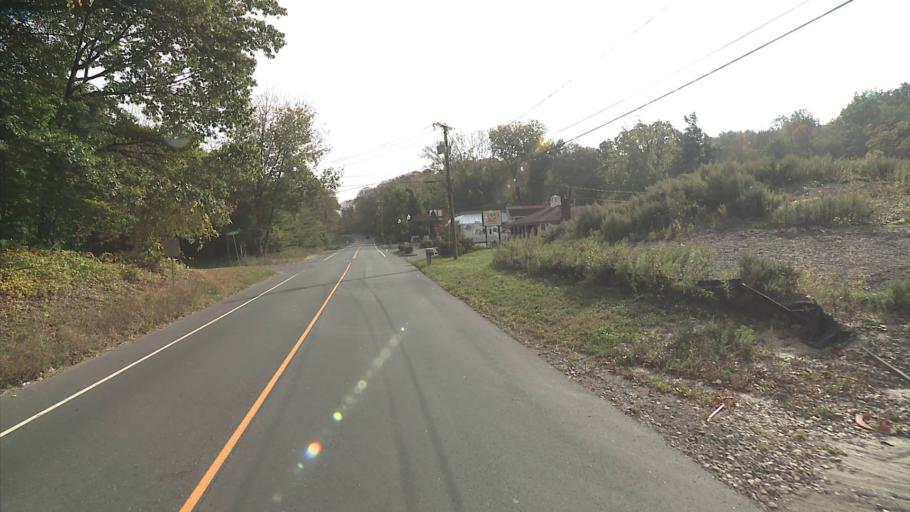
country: US
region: Connecticut
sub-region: Fairfield County
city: Newtown
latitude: 41.4162
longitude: -73.3620
